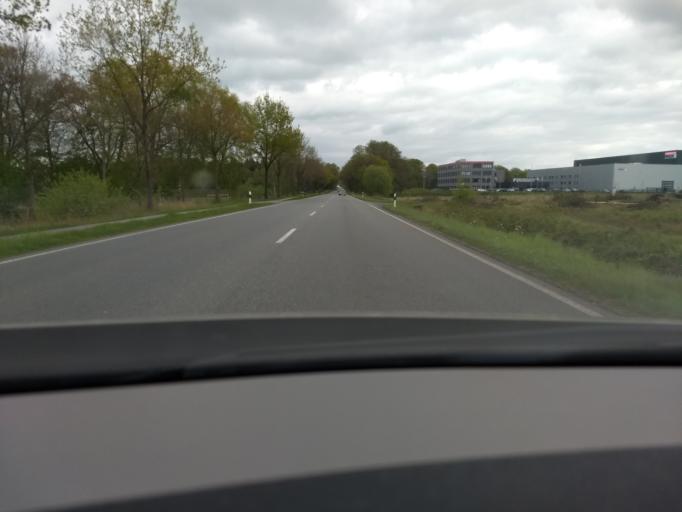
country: DE
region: Lower Saxony
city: Rastede
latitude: 53.2233
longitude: 8.2455
